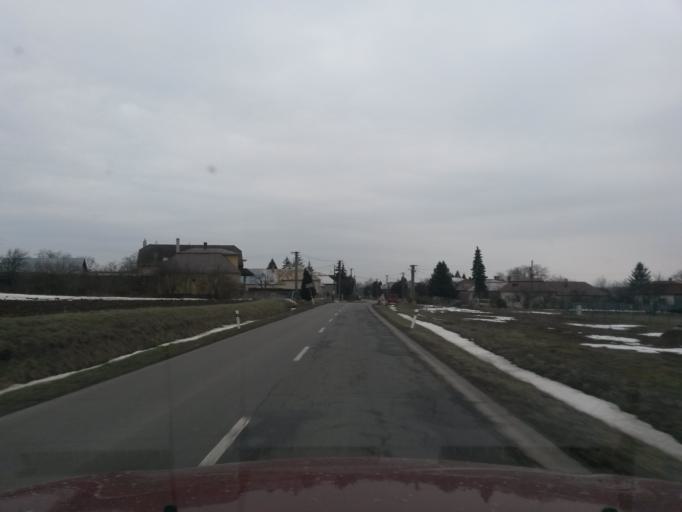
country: SK
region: Kosicky
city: Trebisov
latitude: 48.6896
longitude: 21.8103
